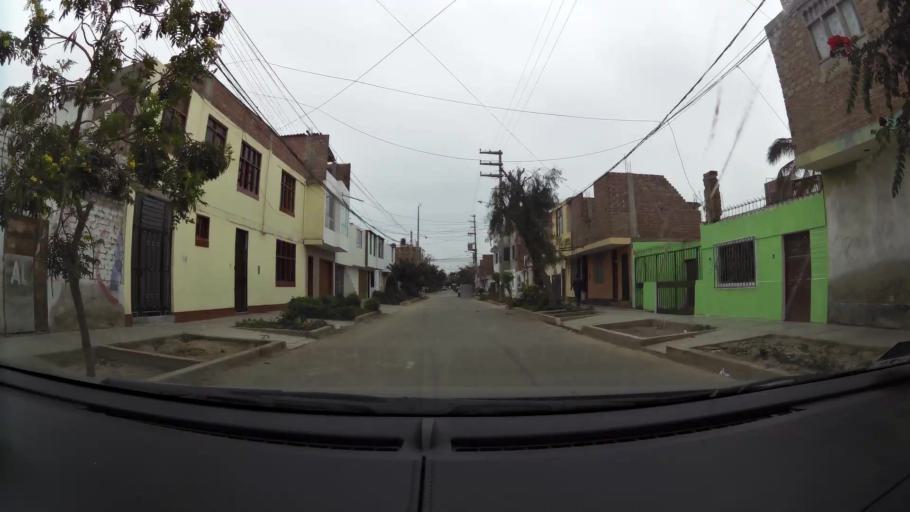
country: PE
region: La Libertad
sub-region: Provincia de Trujillo
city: Buenos Aires
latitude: -8.1372
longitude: -79.0461
